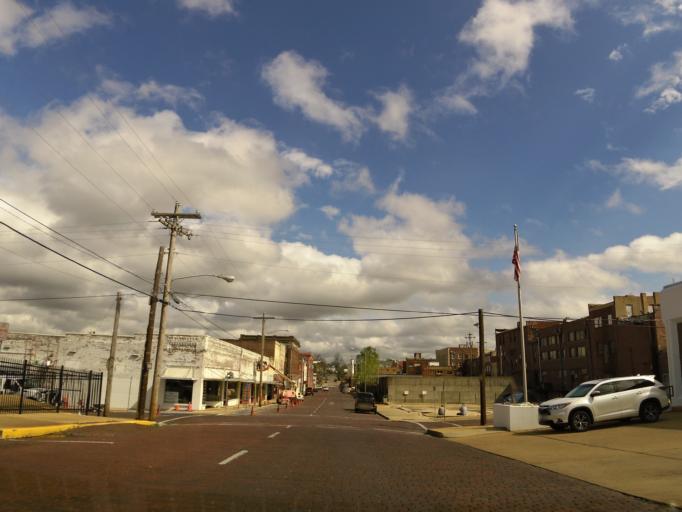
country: US
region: Missouri
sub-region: Butler County
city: Poplar Bluff
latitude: 36.7546
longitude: -90.3943
